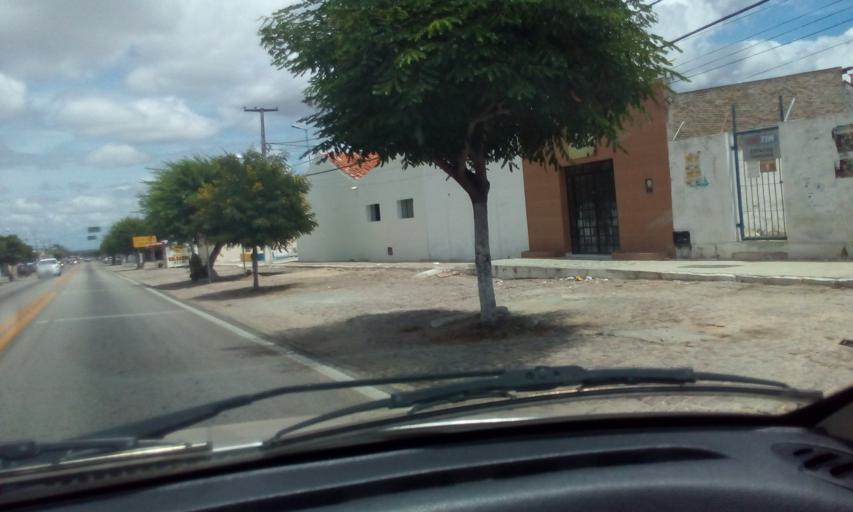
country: BR
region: Rio Grande do Norte
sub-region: Tangara
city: Tangara
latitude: -6.2010
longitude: -35.8027
